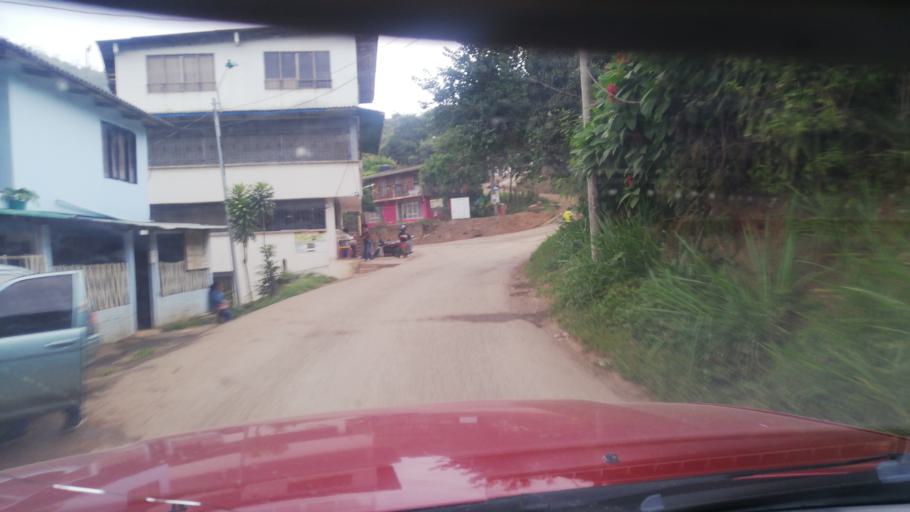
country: CO
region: Valle del Cauca
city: Cali
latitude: 3.4978
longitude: -76.5494
